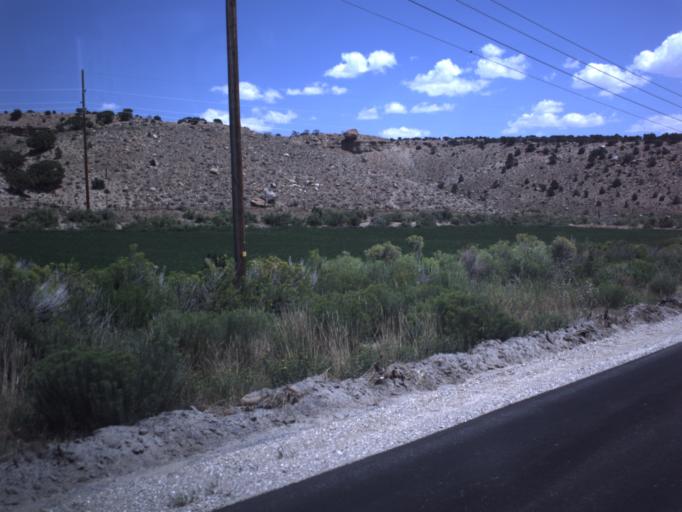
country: US
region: Utah
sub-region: Emery County
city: Orangeville
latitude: 39.2651
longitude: -111.1259
